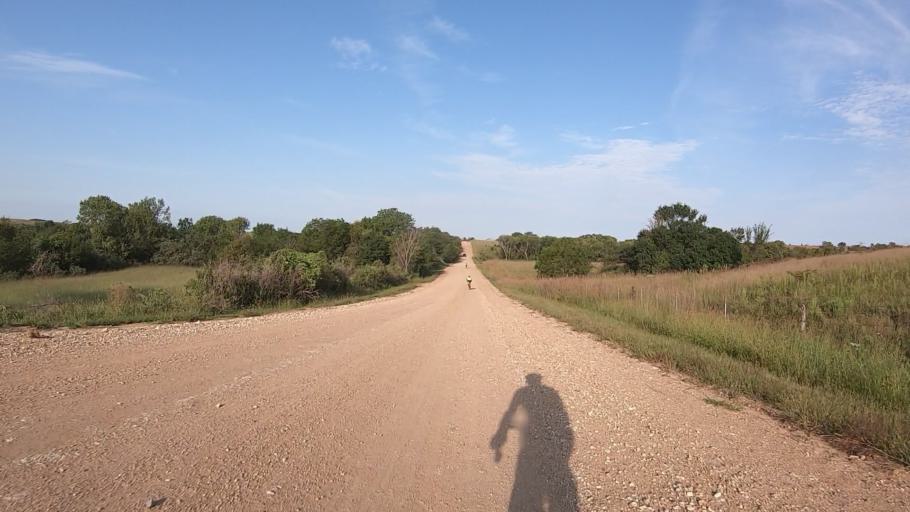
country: US
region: Kansas
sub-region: Marshall County
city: Blue Rapids
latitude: 39.6750
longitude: -96.7889
